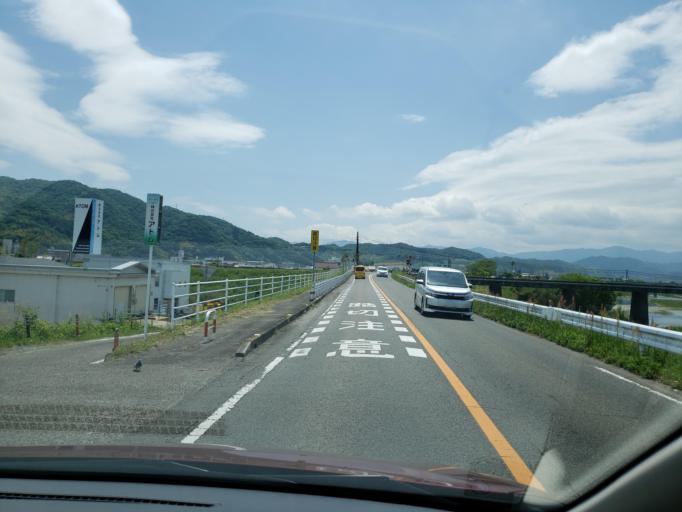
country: JP
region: Tokushima
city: Tokushima-shi
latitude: 34.0778
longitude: 134.5020
